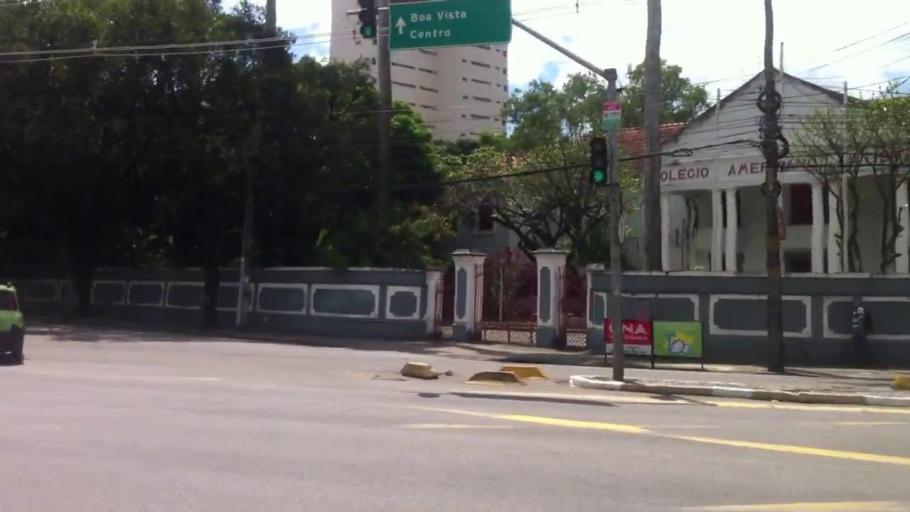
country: BR
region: Pernambuco
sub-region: Recife
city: Recife
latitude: -8.0522
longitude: -34.8947
